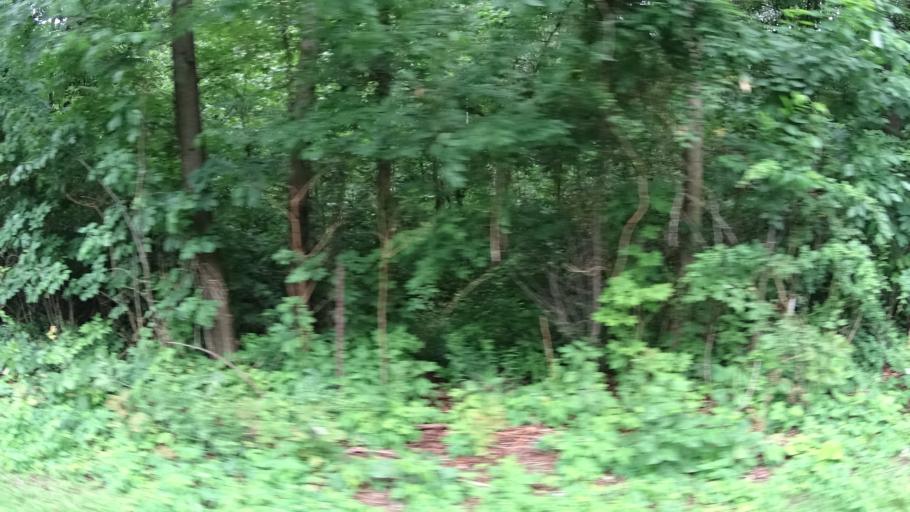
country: US
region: Ohio
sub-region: Erie County
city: Milan
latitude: 41.2856
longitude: -82.5431
